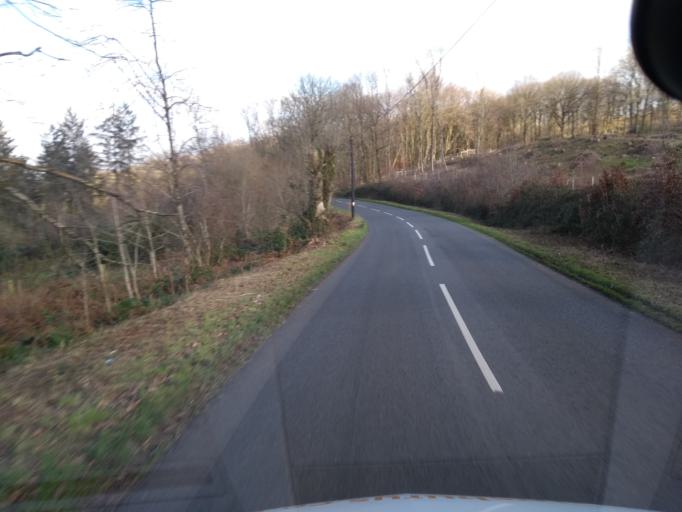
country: GB
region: England
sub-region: Somerset
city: Creech Saint Michael
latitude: 50.9393
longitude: -3.0438
